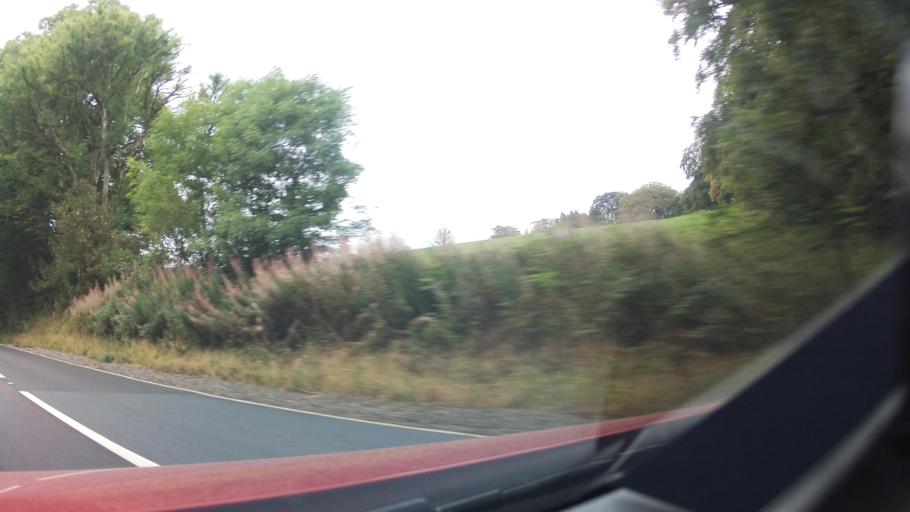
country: GB
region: Scotland
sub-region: Dumfries and Galloway
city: Moffat
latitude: 55.2332
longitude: -3.4620
